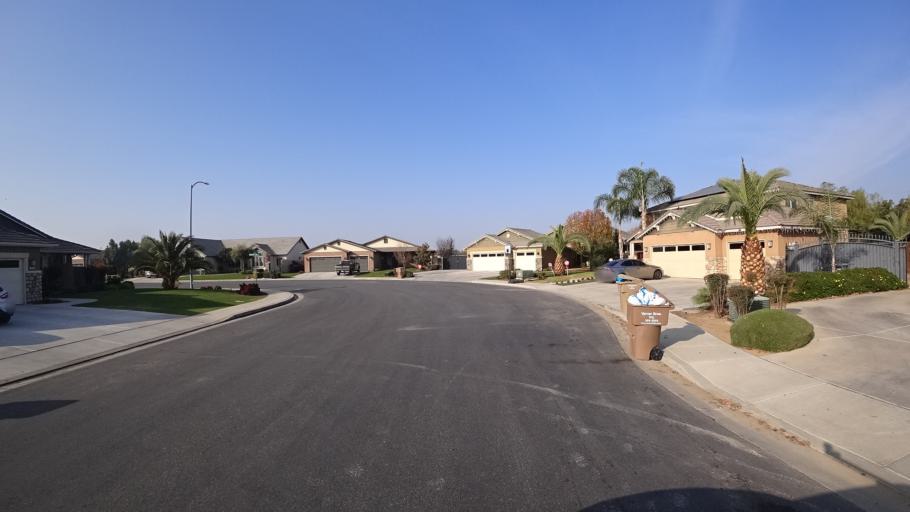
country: US
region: California
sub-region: Kern County
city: Greenacres
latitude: 35.4353
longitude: -119.1215
